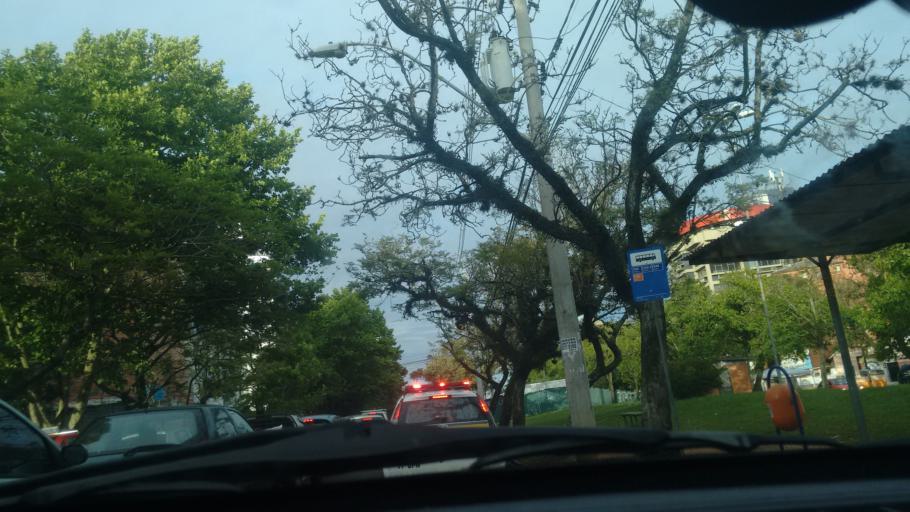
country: BR
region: Rio Grande do Sul
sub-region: Porto Alegre
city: Porto Alegre
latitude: -30.0210
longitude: -51.1819
